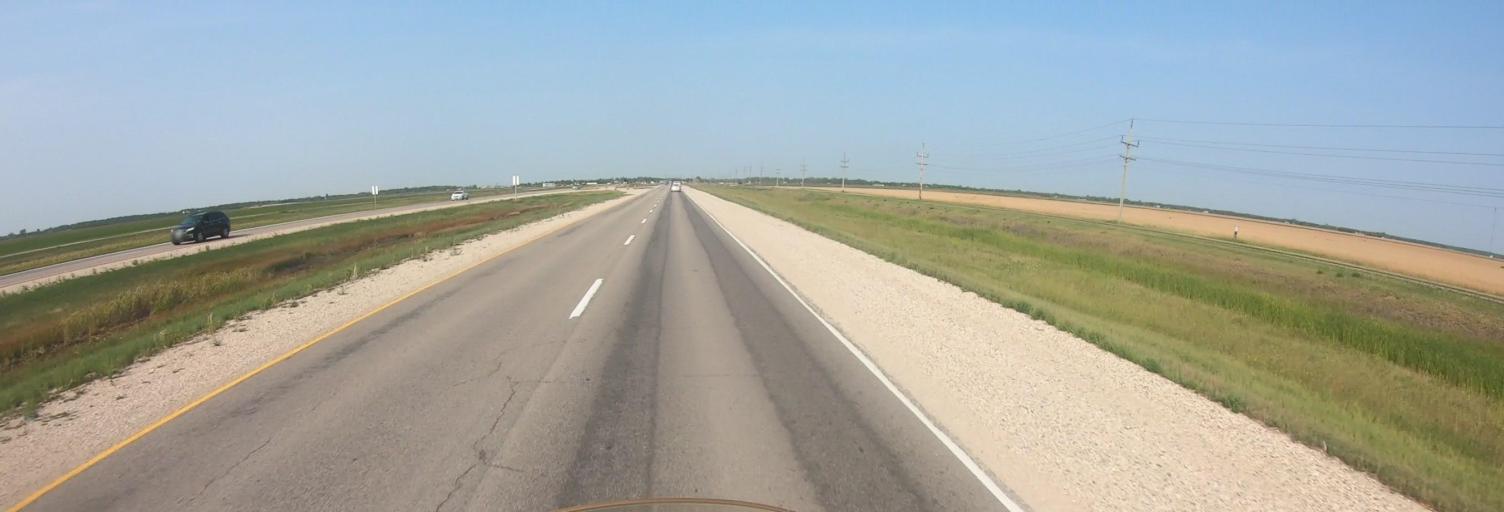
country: CA
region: Manitoba
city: Steinbach
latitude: 49.6493
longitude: -96.6773
